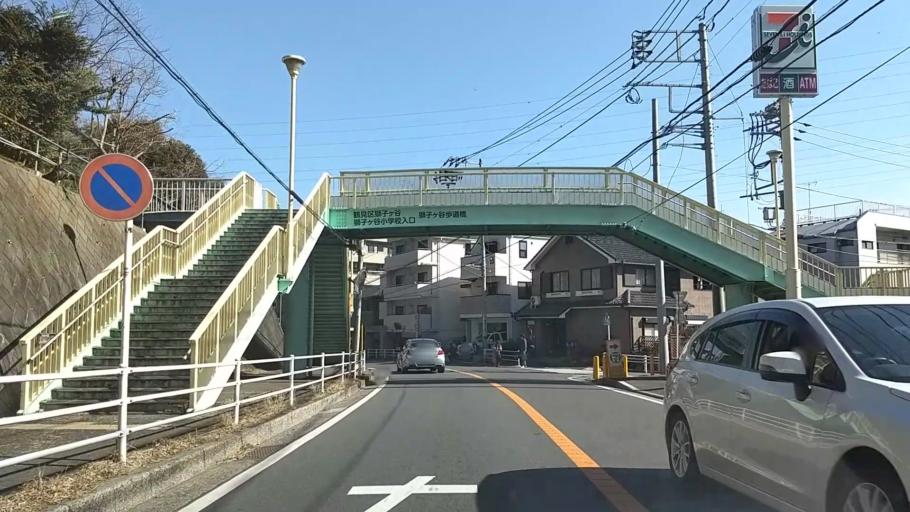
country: JP
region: Kanagawa
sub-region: Kawasaki-shi
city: Kawasaki
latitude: 35.5177
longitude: 139.6489
